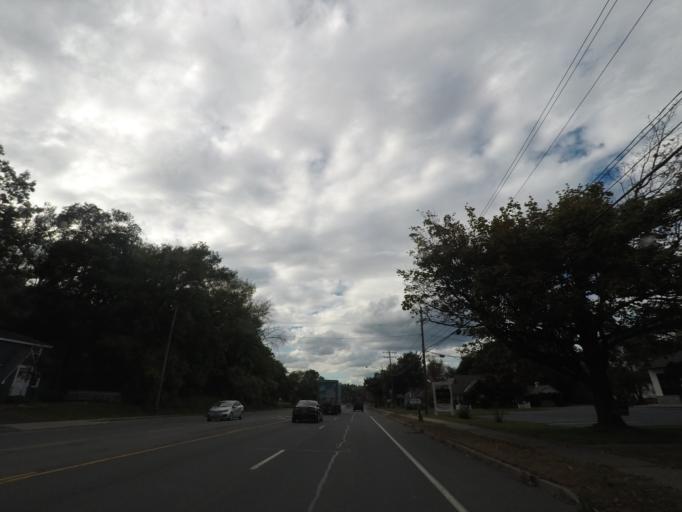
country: US
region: New York
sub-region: Albany County
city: Westmere
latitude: 42.6918
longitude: -73.8711
